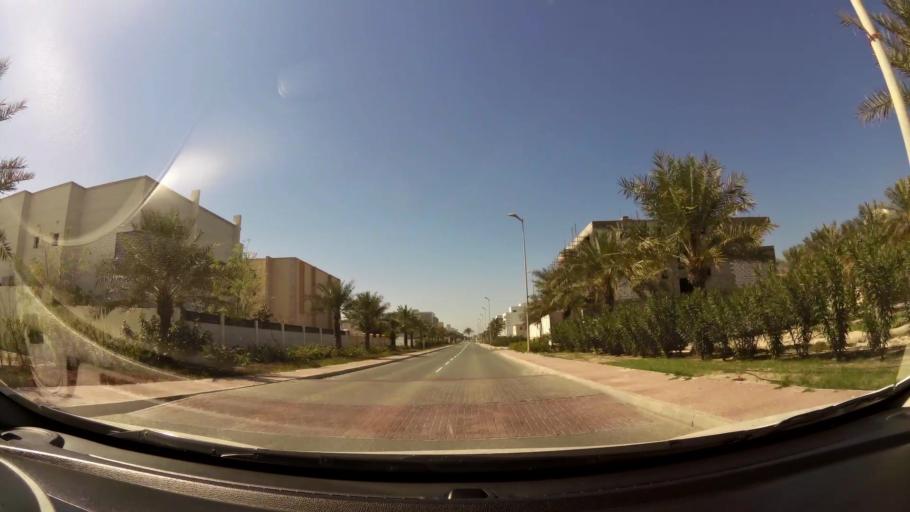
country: BH
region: Muharraq
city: Al Hadd
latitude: 26.2968
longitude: 50.6707
